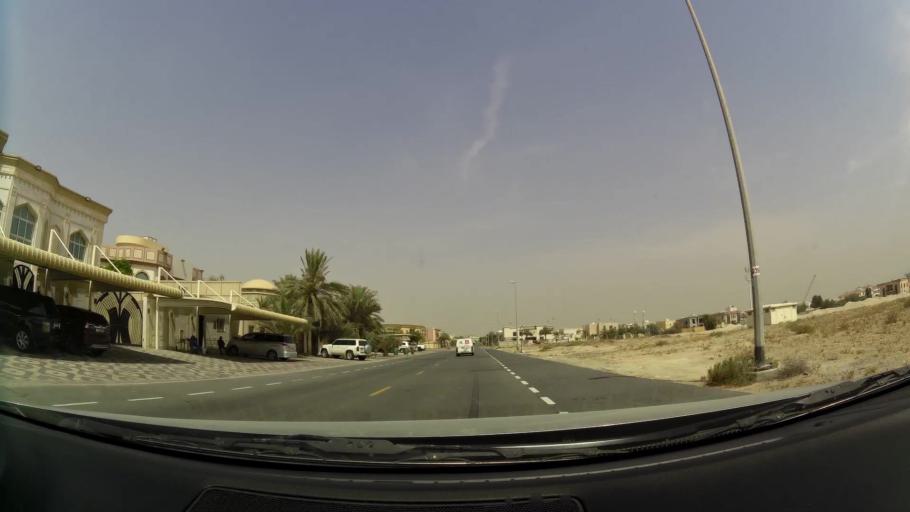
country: AE
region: Ash Shariqah
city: Sharjah
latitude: 25.2423
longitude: 55.4352
